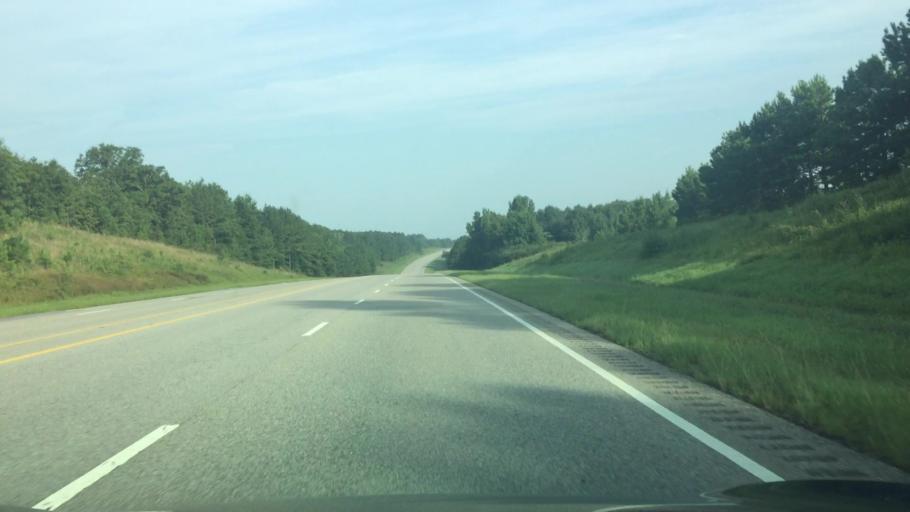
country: US
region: Alabama
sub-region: Covington County
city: Andalusia
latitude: 31.4468
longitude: -86.6194
